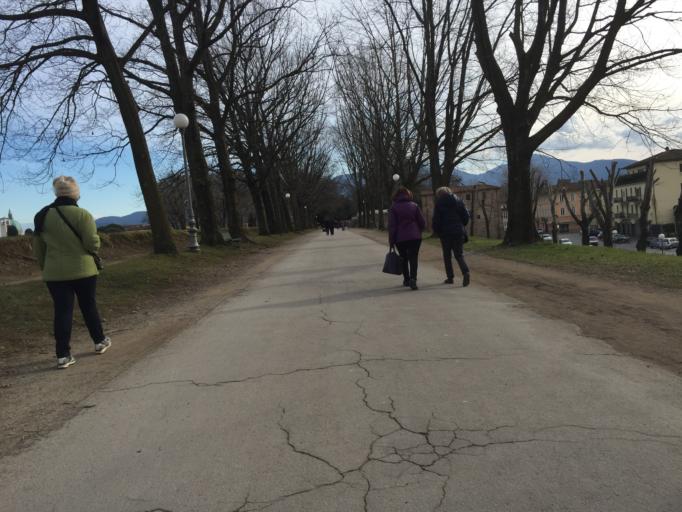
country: IT
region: Tuscany
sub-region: Provincia di Lucca
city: Lucca
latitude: 43.8471
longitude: 10.5142
